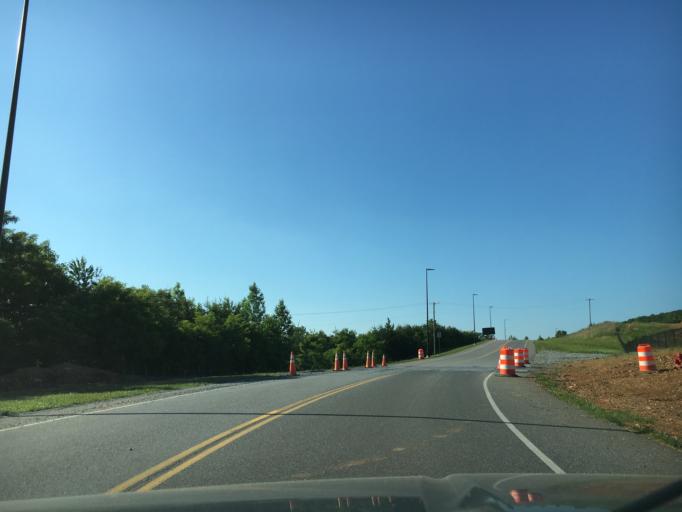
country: US
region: Virginia
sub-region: City of Lynchburg
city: West Lynchburg
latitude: 37.3392
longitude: -79.1781
